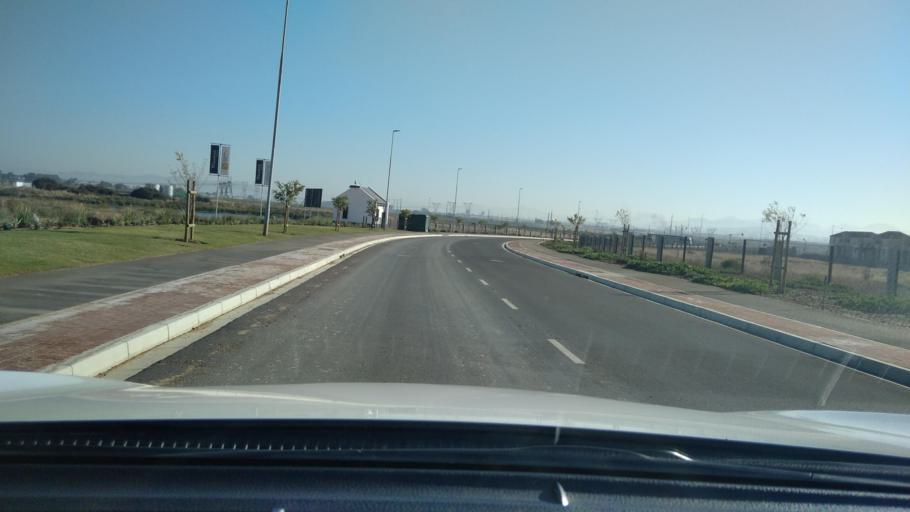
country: ZA
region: Western Cape
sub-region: City of Cape Town
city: Kraaifontein
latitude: -33.8107
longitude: 18.6915
